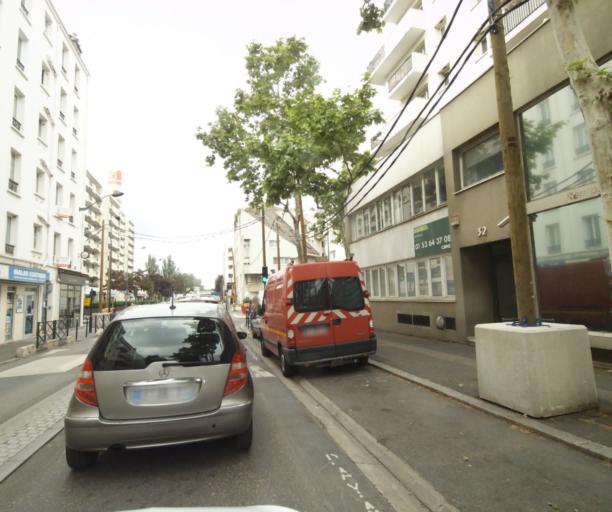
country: FR
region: Ile-de-France
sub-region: Departement des Hauts-de-Seine
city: Clichy
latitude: 48.9040
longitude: 2.2996
